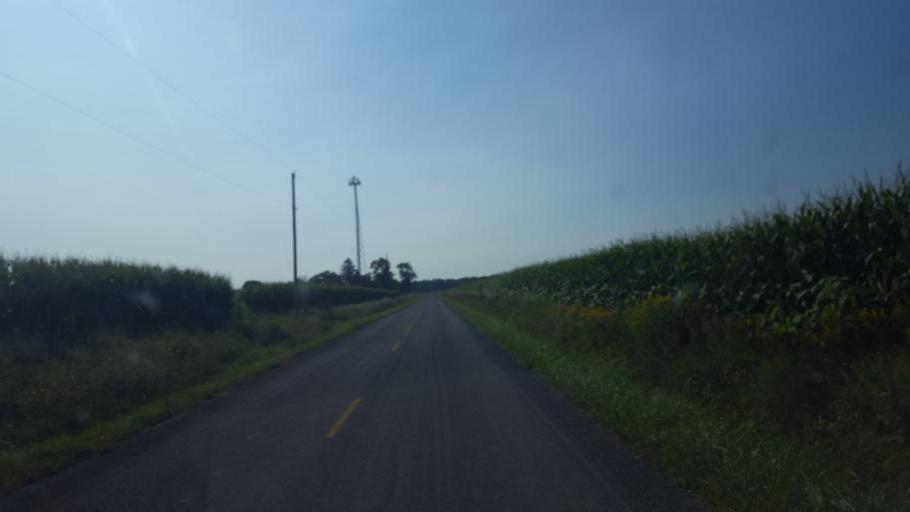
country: US
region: Ohio
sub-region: Ashtabula County
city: Orwell
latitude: 41.4730
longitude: -80.8843
